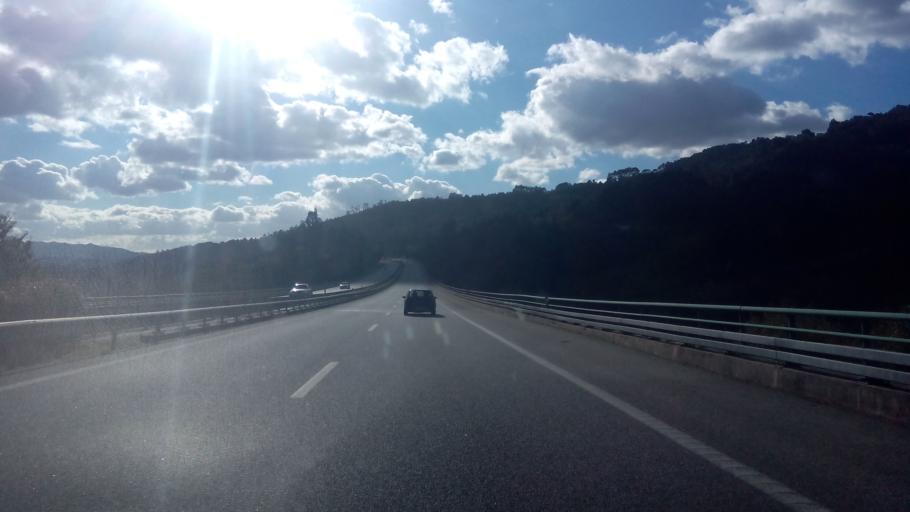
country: PT
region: Porto
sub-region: Amarante
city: Amarante
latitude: 41.2445
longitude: -8.1129
